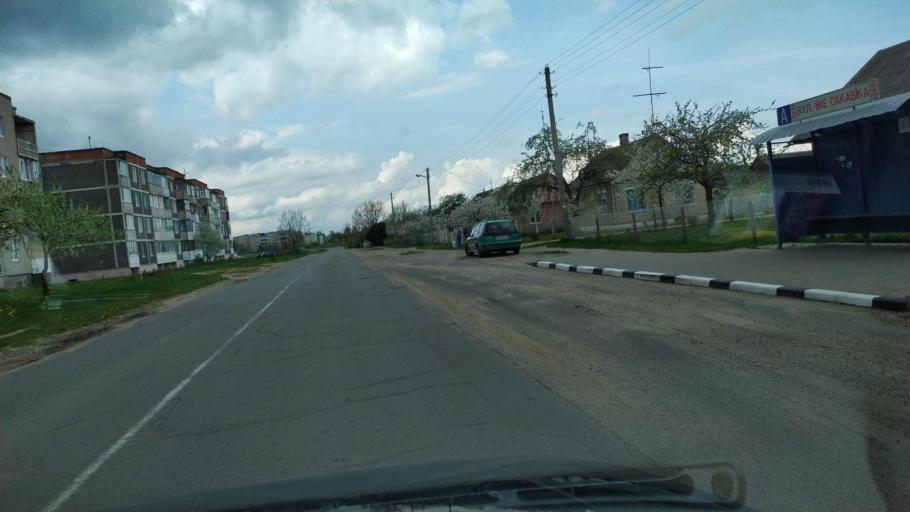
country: BY
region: Brest
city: Pruzhany
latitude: 52.5605
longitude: 24.4262
